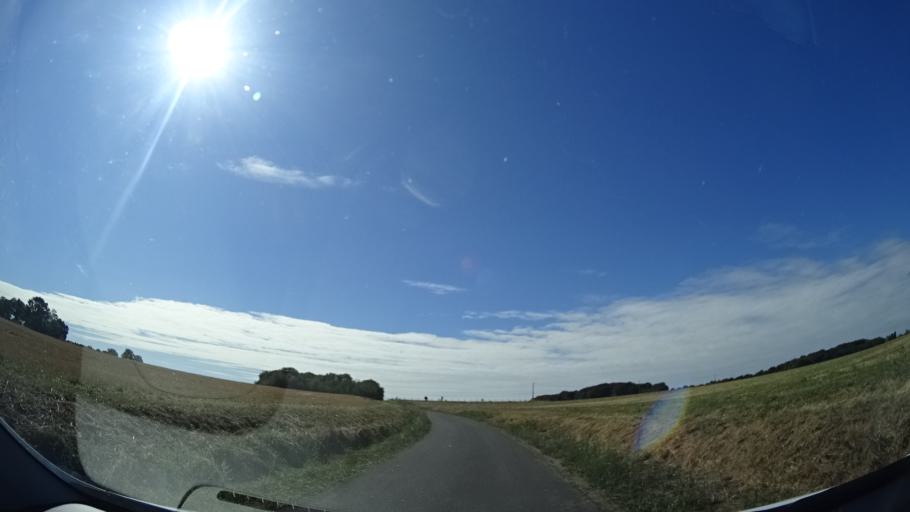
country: FR
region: Centre
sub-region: Departement du Loiret
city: Trigueres
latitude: 47.9584
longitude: 2.9747
